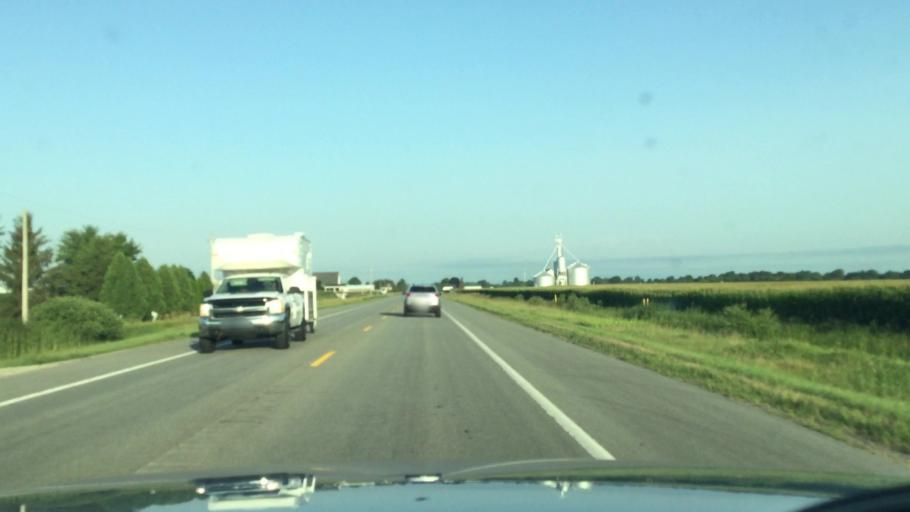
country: US
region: Michigan
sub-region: Gratiot County
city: Ithaca
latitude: 43.1762
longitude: -84.6876
